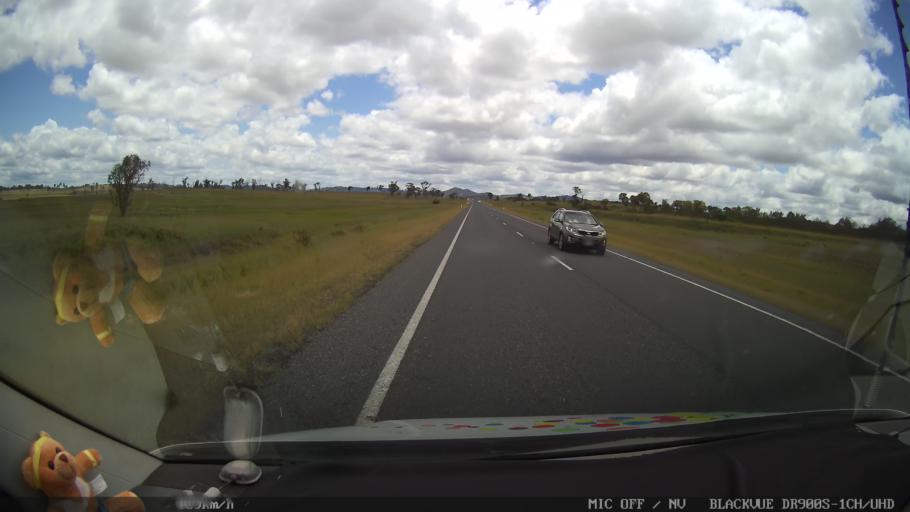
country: AU
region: New South Wales
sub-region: Glen Innes Severn
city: Glen Innes
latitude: -29.4100
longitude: 151.8681
